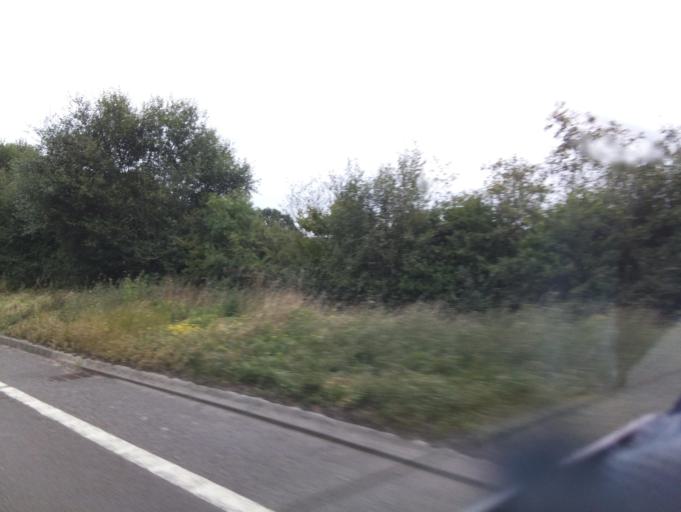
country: GB
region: England
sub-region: Shropshire
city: Stoke upon Tern
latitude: 52.8556
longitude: -2.5556
